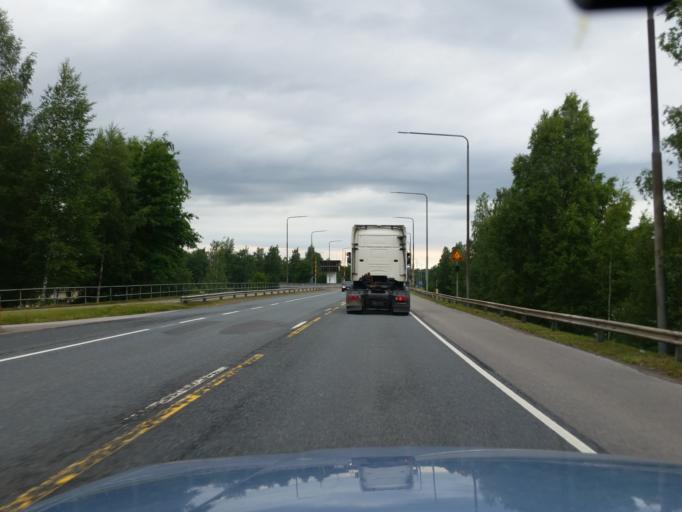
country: FI
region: Uusimaa
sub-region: Raaseporin
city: Ekenaes
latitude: 59.9828
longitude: 23.4308
